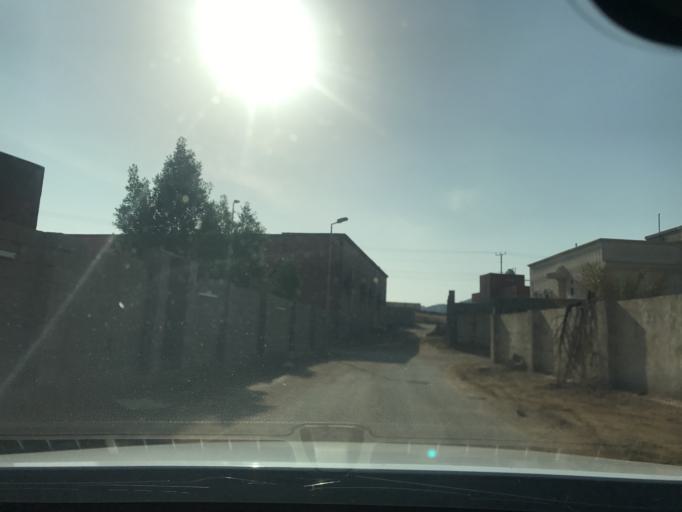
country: SA
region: Makkah
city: Al Jumum
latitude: 21.4525
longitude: 39.5359
